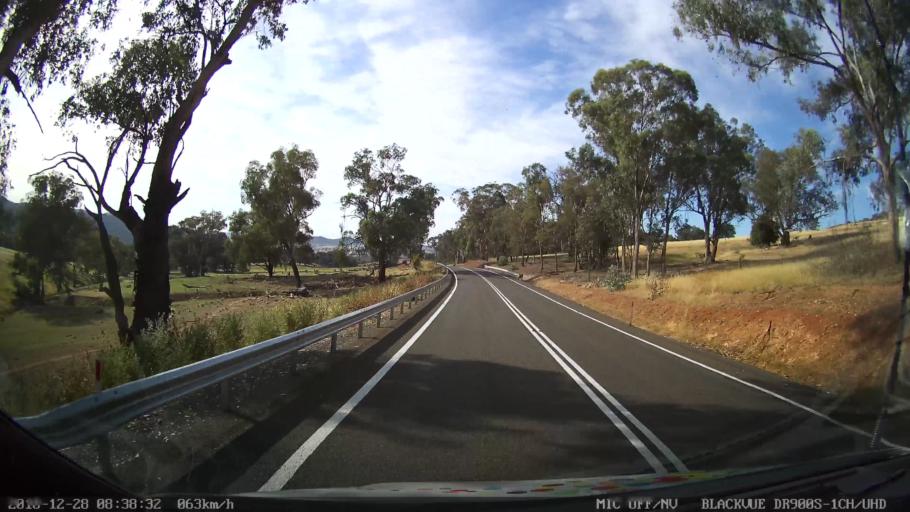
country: AU
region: New South Wales
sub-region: Blayney
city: Blayney
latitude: -34.0045
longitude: 149.3154
